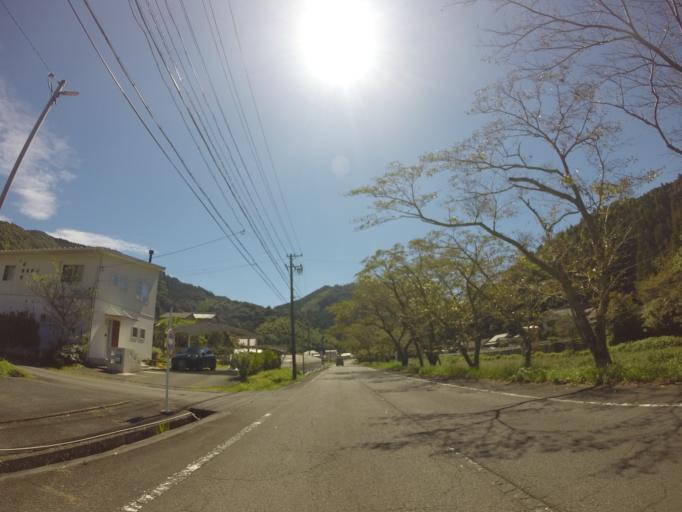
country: JP
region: Shizuoka
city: Fujieda
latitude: 34.9419
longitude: 138.2099
